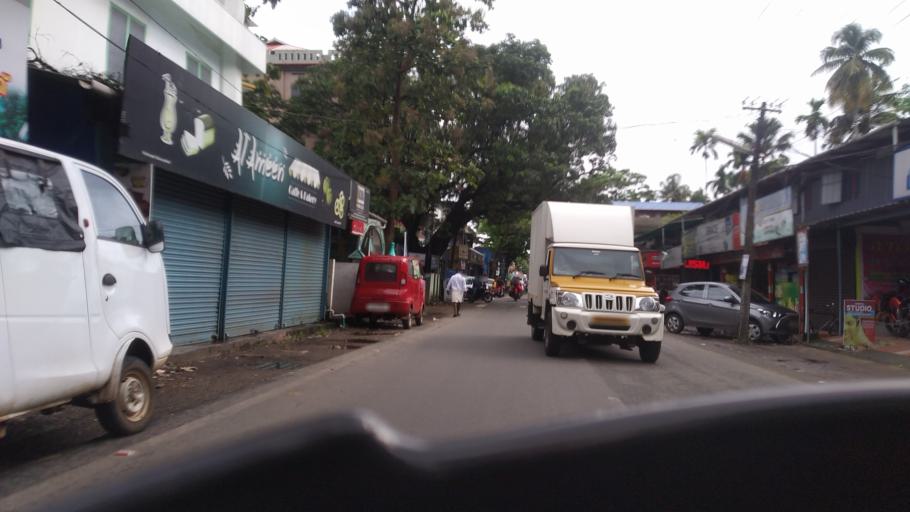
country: IN
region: Kerala
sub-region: Ernakulam
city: Elur
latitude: 10.0907
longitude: 76.2078
